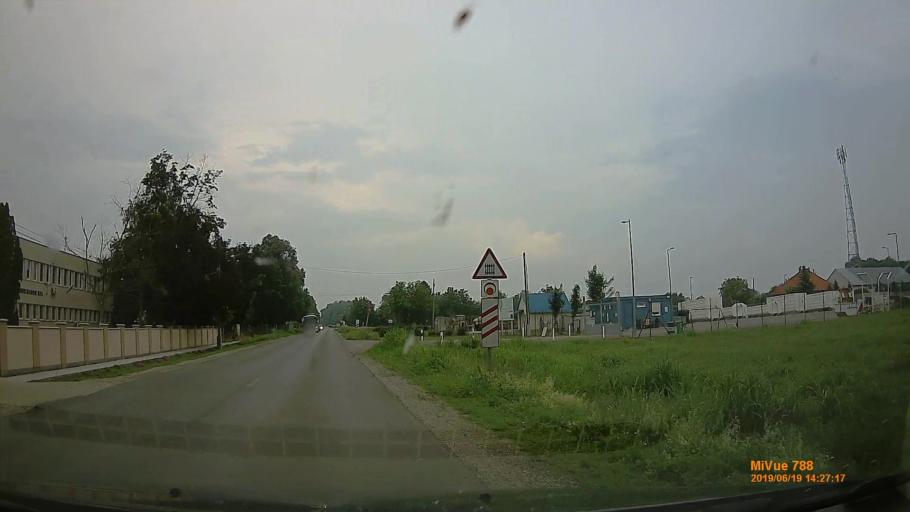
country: HU
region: Baranya
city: Szigetvar
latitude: 46.0415
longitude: 17.7821
